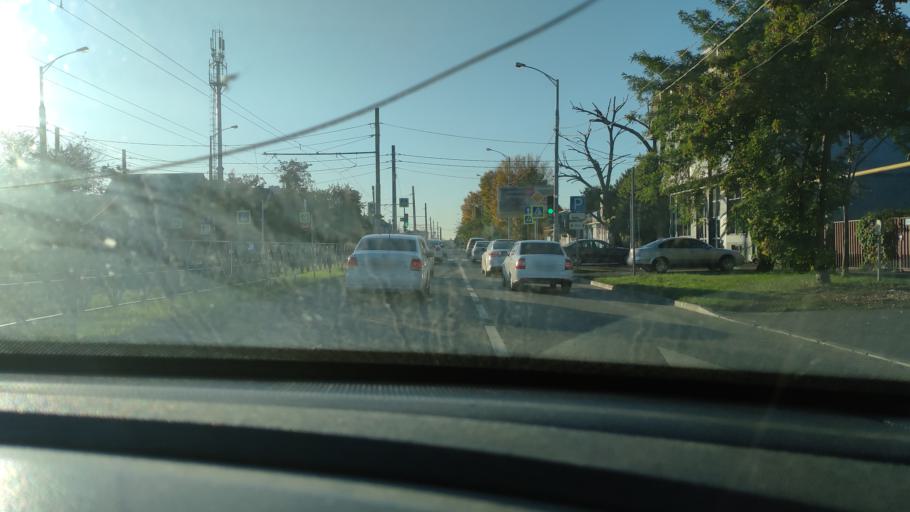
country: RU
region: Krasnodarskiy
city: Krasnodar
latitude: 45.0394
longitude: 38.9607
